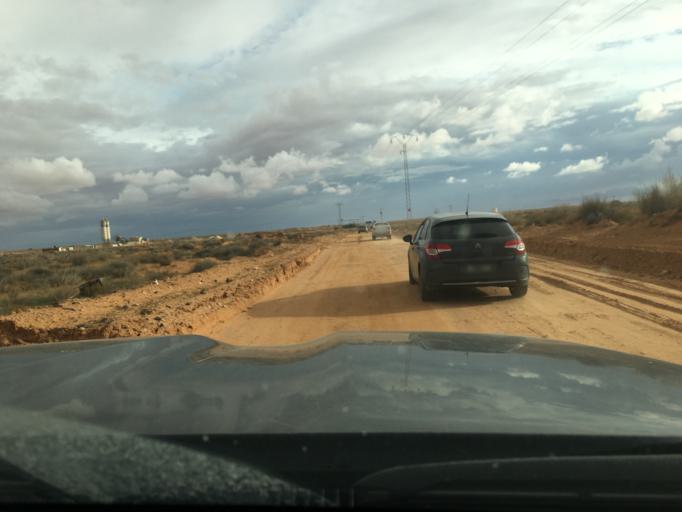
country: TN
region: Madanin
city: Medenine
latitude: 33.2702
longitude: 10.5681
